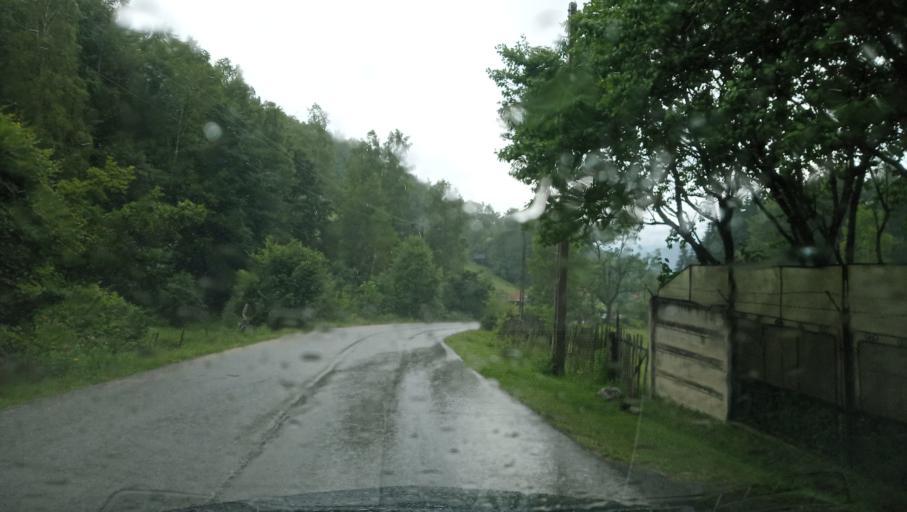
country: RO
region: Hunedoara
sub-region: Oras Petrila
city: Petrila
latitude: 45.3978
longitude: 23.4183
